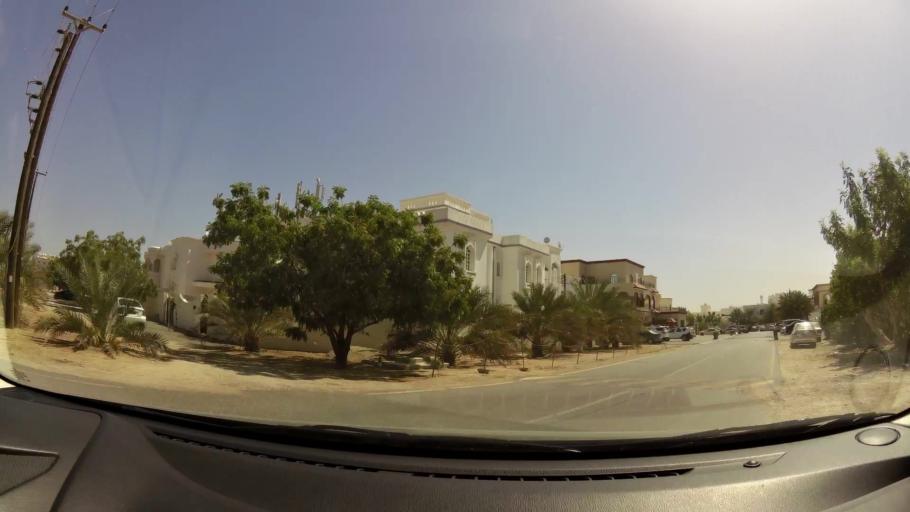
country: OM
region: Muhafazat Masqat
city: As Sib al Jadidah
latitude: 23.5927
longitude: 58.2426
